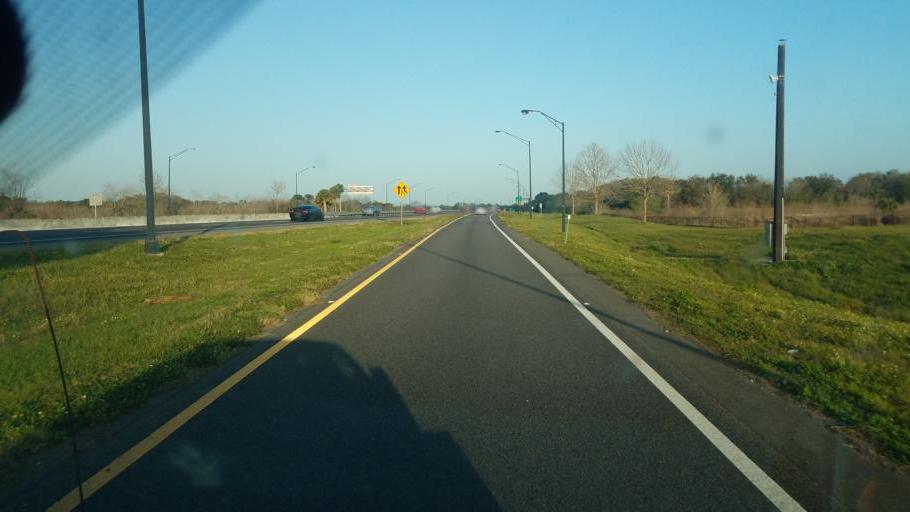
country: US
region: Florida
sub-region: Polk County
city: Crystal Lake
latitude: 27.9962
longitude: -81.9190
